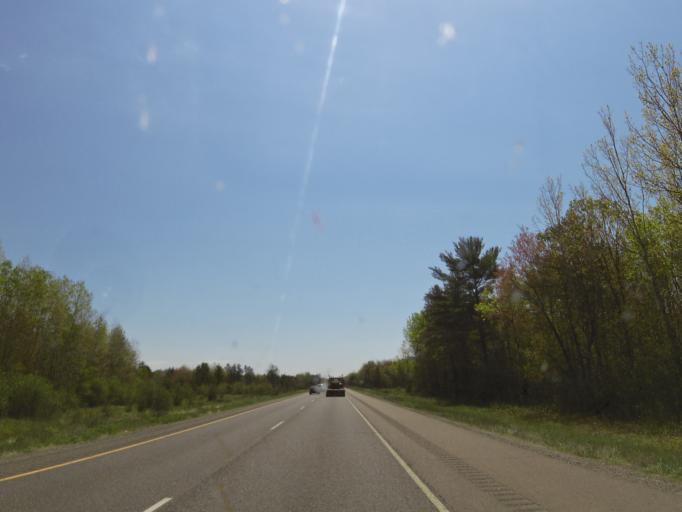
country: US
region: Wisconsin
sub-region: Jackson County
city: Black River Falls
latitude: 44.2590
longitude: -90.7671
